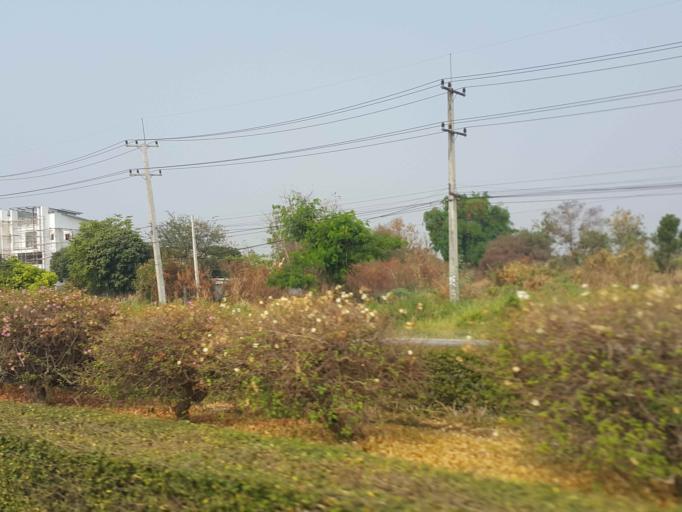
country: TH
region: Chiang Mai
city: Saraphi
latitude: 18.7495
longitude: 99.0696
